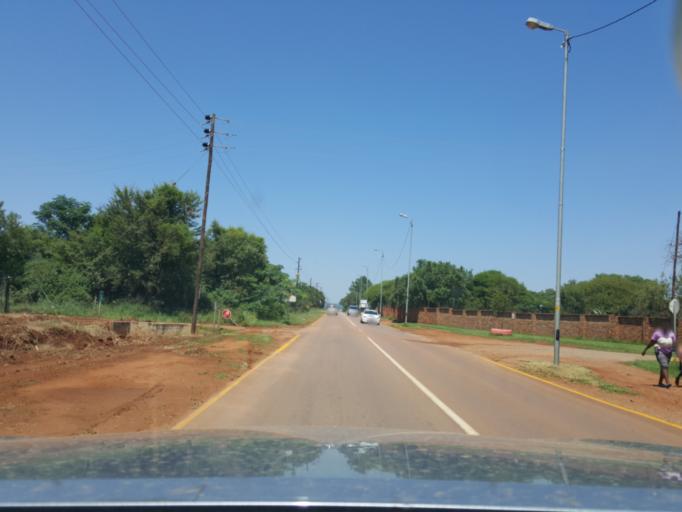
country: ZA
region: Gauteng
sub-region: City of Tshwane Metropolitan Municipality
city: Pretoria
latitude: -25.6720
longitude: 28.3041
